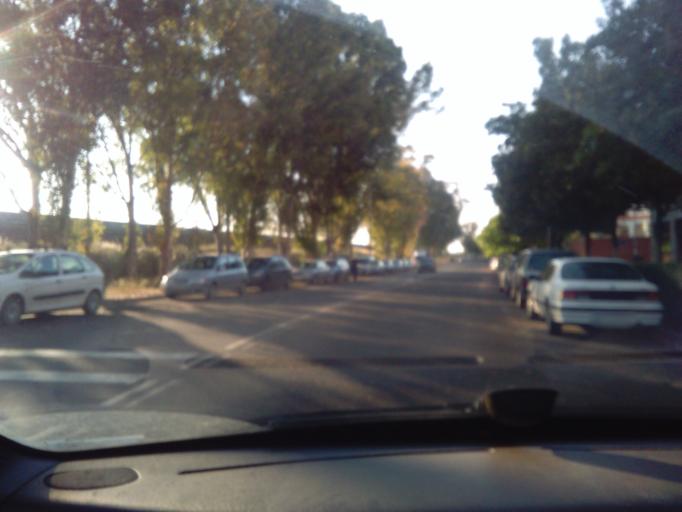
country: ES
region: Andalusia
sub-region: Provincia de Sevilla
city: Sevilla
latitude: 37.4065
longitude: -5.9372
